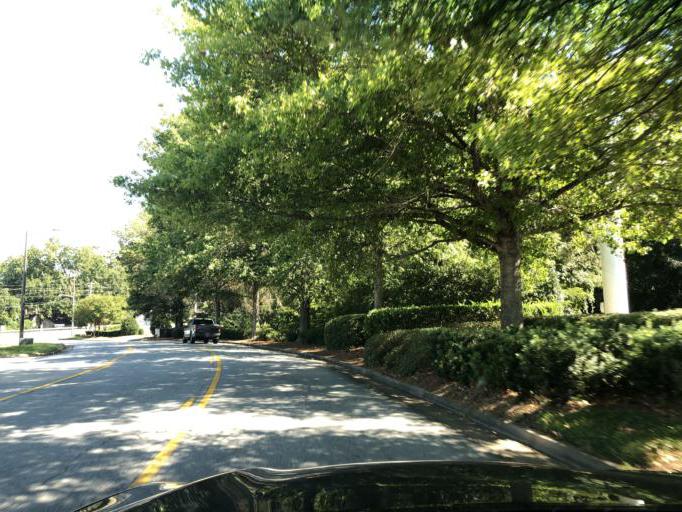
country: US
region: Georgia
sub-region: Muscogee County
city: Columbus
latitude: 32.5162
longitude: -84.9536
